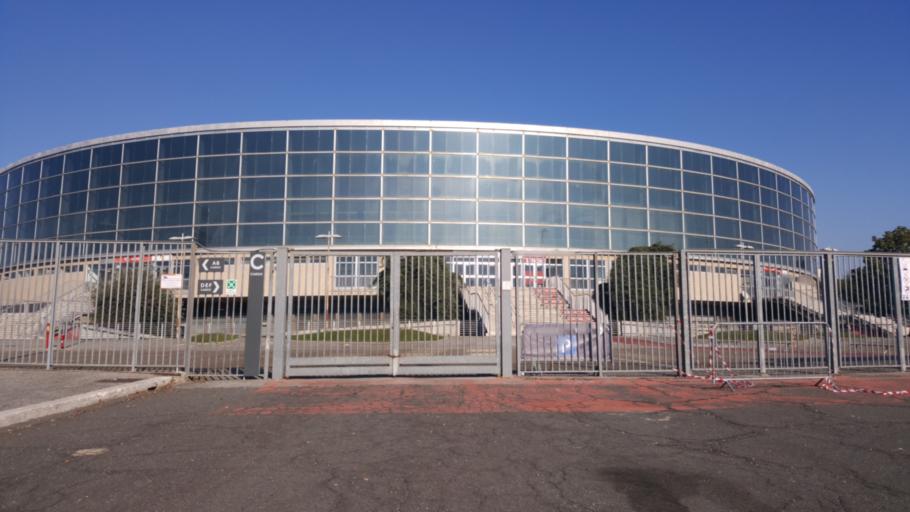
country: IT
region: Latium
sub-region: Citta metropolitana di Roma Capitale
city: Selcetta
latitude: 41.8244
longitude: 12.4658
